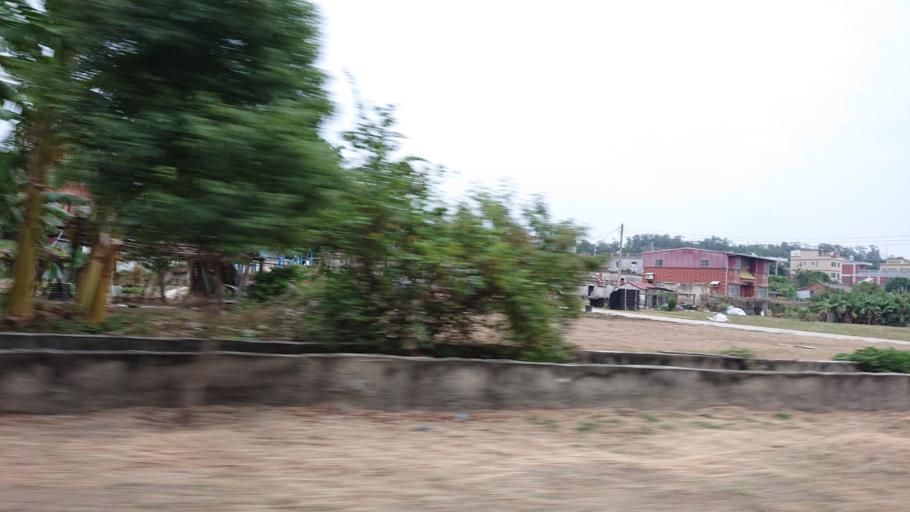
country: TW
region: Fukien
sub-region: Kinmen
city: Jincheng
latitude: 24.4273
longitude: 118.2289
